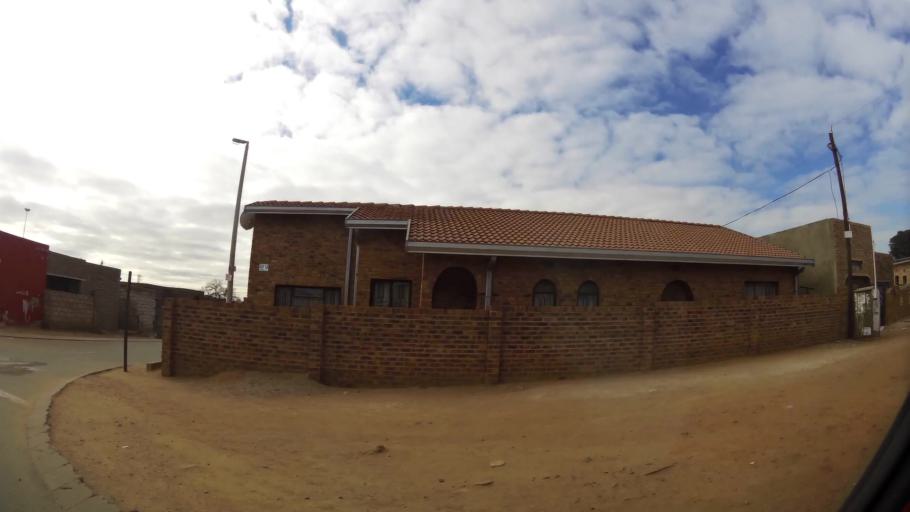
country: ZA
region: Gauteng
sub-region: City of Johannesburg Metropolitan Municipality
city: Modderfontein
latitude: -26.0470
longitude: 28.1844
